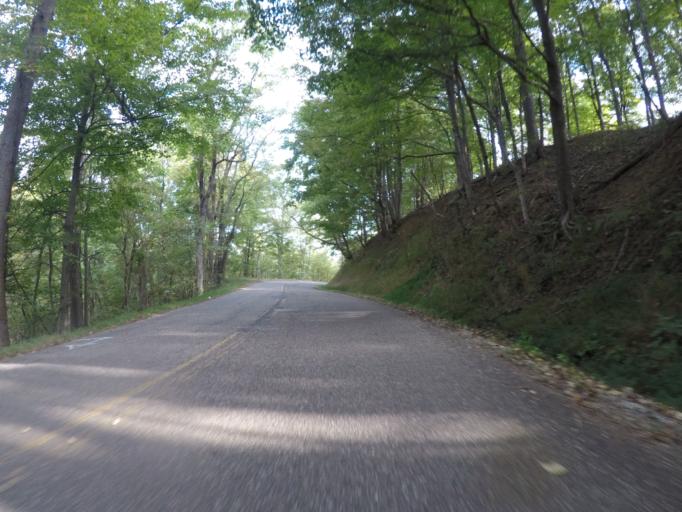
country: US
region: West Virginia
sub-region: Cabell County
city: Lesage
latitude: 38.5790
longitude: -82.4286
